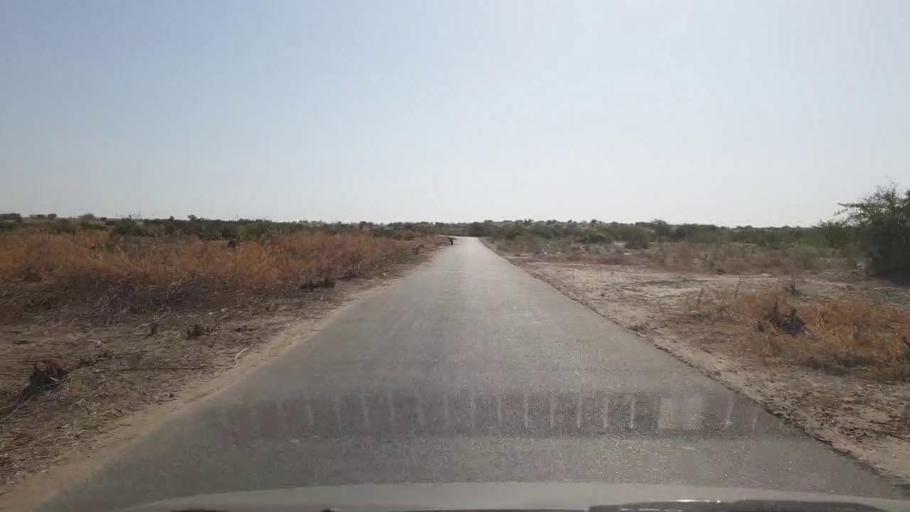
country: PK
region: Sindh
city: Chor
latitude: 25.4888
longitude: 69.7846
